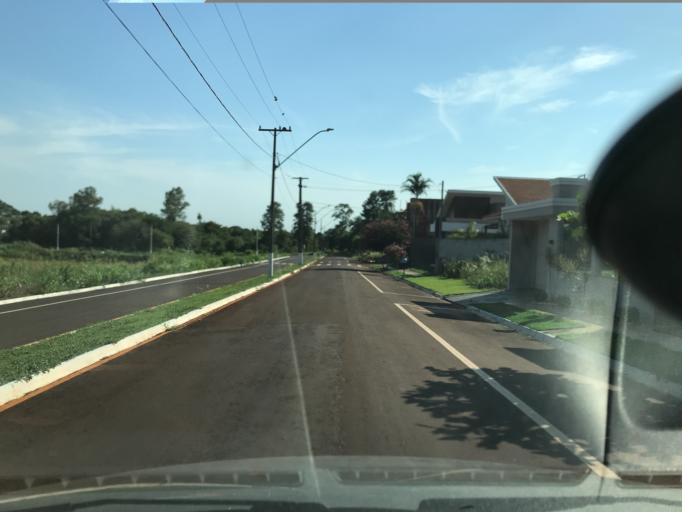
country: BR
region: Parana
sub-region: Palotina
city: Palotina
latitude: -24.2889
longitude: -53.8291
